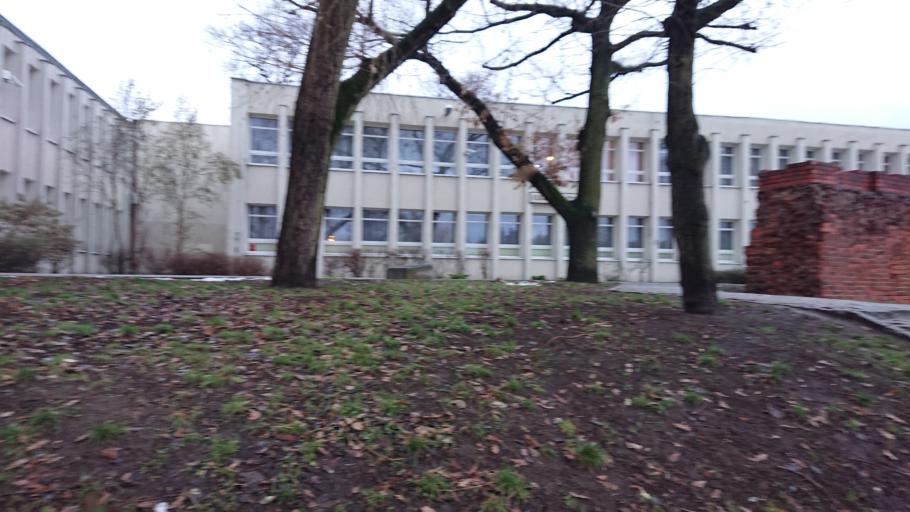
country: PL
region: Kujawsko-Pomorskie
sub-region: Powiat inowroclawski
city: Inowroclaw
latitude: 52.7974
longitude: 18.2604
